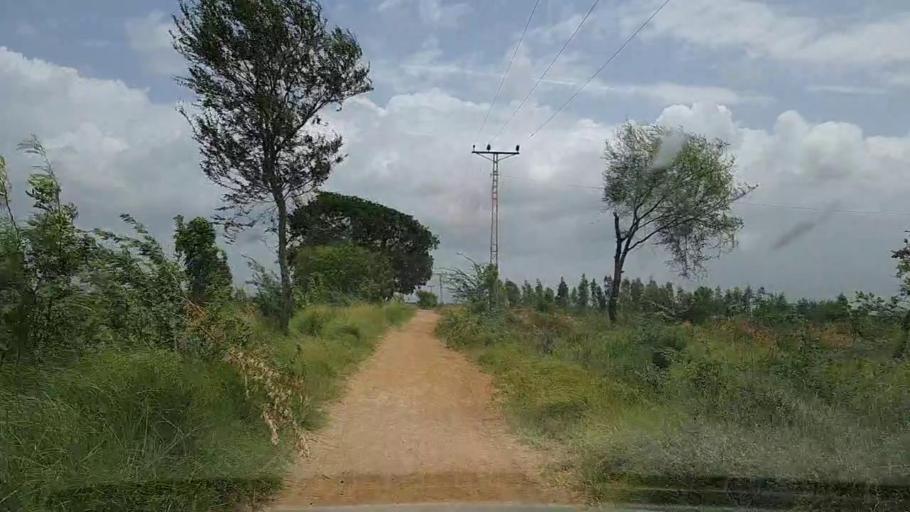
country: PK
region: Sindh
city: Thatta
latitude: 24.6071
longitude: 68.0339
